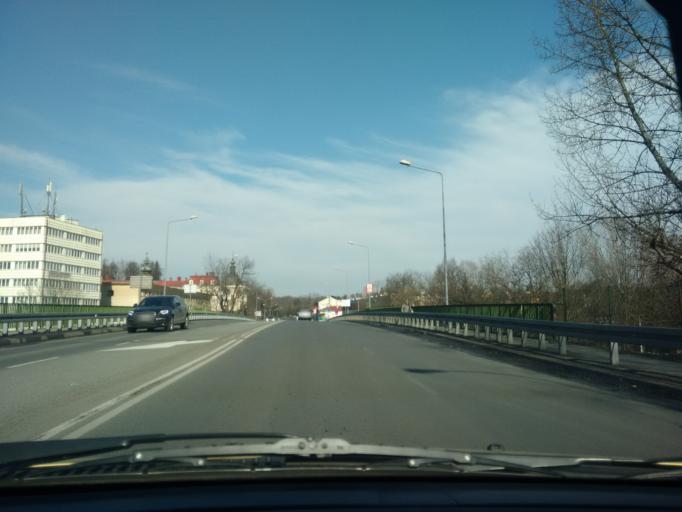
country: PL
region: Silesian Voivodeship
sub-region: Powiat cieszynski
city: Cieszyn
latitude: 49.7501
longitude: 18.6404
